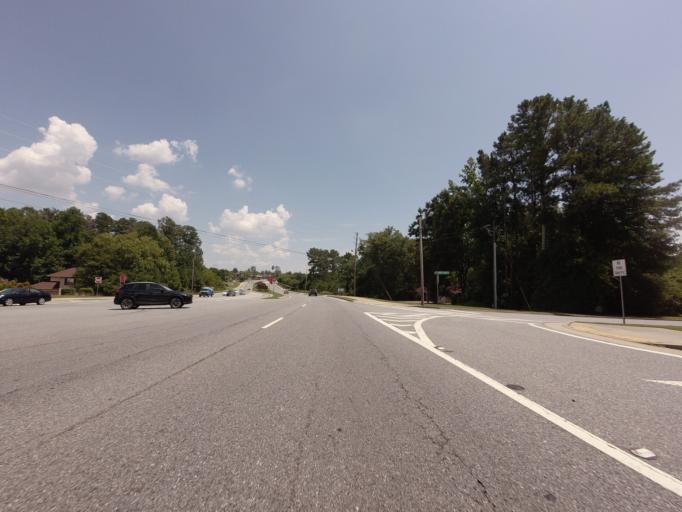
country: US
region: Georgia
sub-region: Fulton County
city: Johns Creek
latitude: 34.0515
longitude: -84.2283
